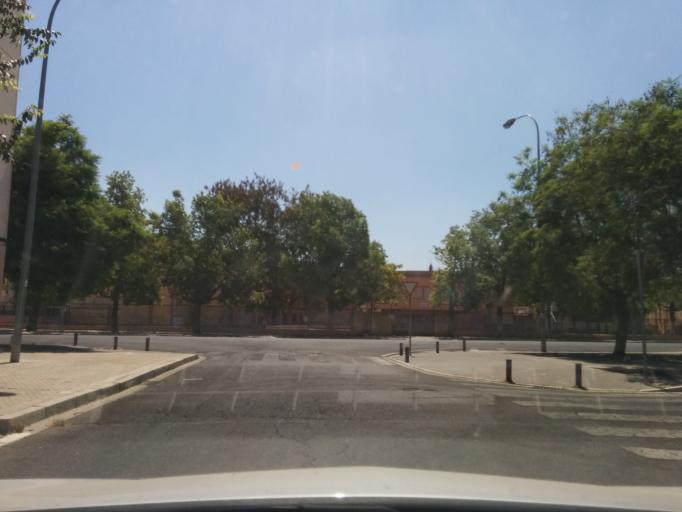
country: ES
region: Andalusia
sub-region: Provincia de Sevilla
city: Sevilla
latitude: 37.3636
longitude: -5.9694
